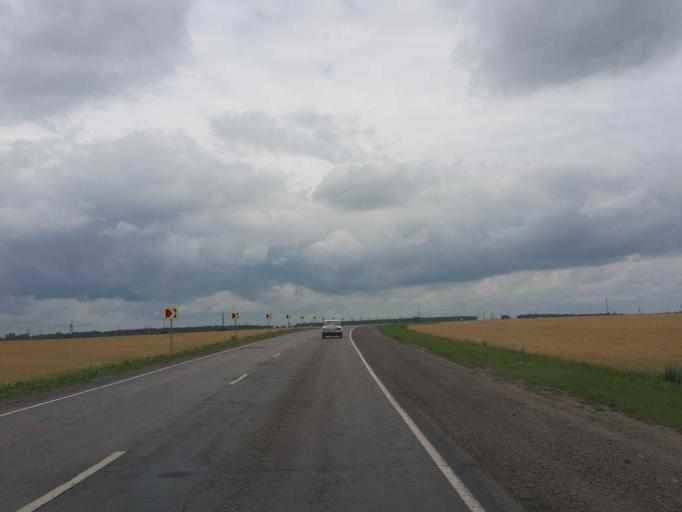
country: RU
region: Tambov
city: Komsomolets
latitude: 52.7508
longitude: 41.2962
